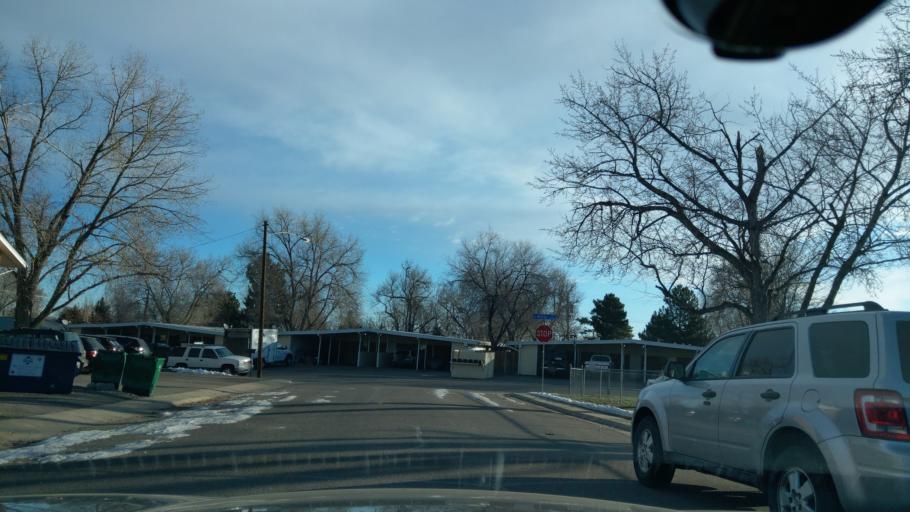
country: US
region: Colorado
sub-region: Jefferson County
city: Lakewood
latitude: 39.7291
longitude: -105.1154
